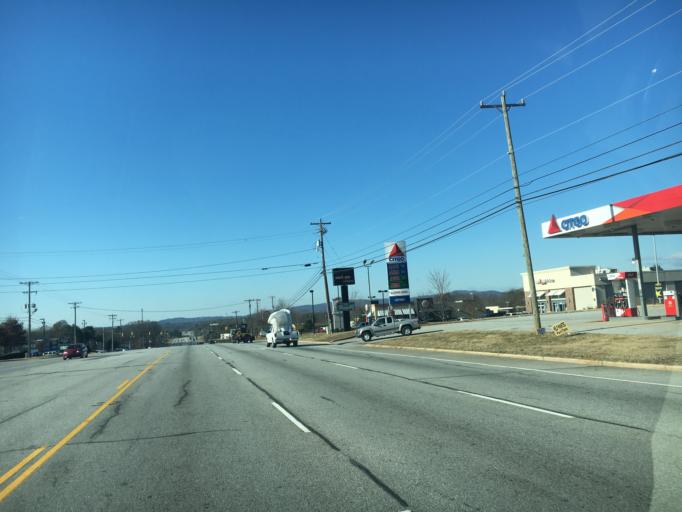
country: US
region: South Carolina
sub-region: Greenville County
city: Taylors
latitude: 34.9361
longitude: -82.2759
